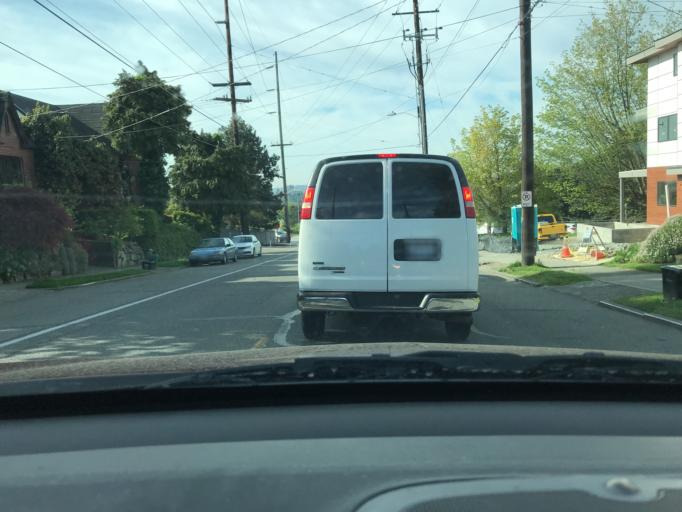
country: US
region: Washington
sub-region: King County
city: Shoreline
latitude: 47.6858
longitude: -122.3231
